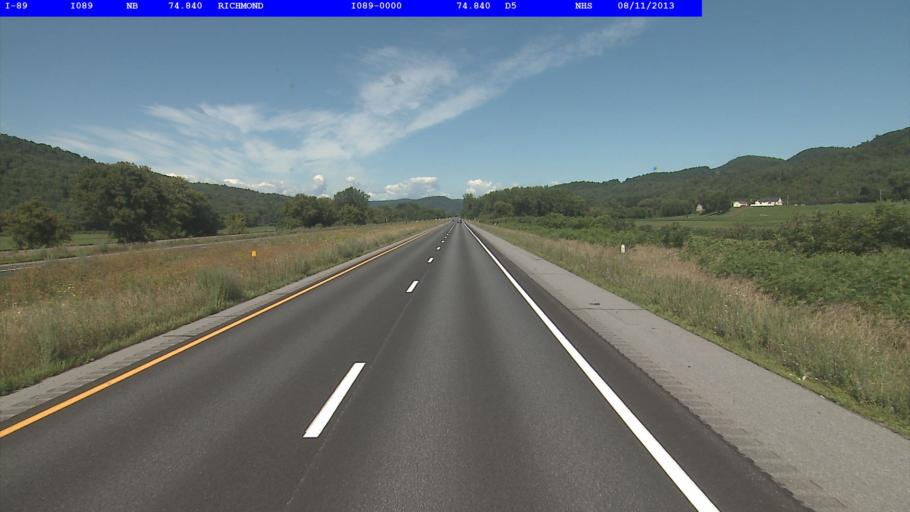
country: US
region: Vermont
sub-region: Chittenden County
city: Jericho
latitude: 44.3926
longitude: -72.9588
